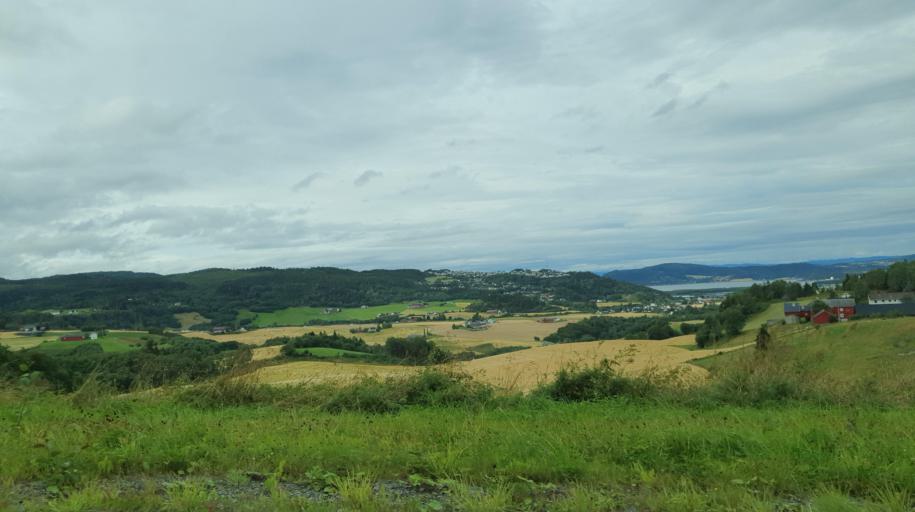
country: NO
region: Nord-Trondelag
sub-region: Stjordal
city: Stjordalshalsen
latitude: 63.4255
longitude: 10.9580
